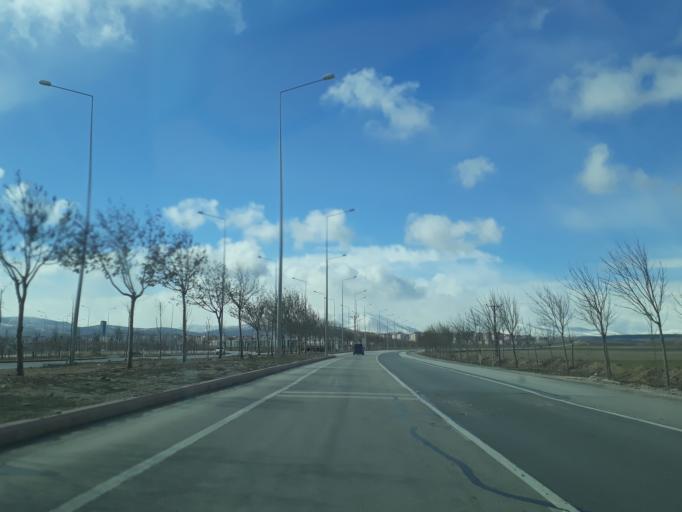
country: TR
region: Konya
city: Asagipinarbasi
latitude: 38.0049
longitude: 32.5556
